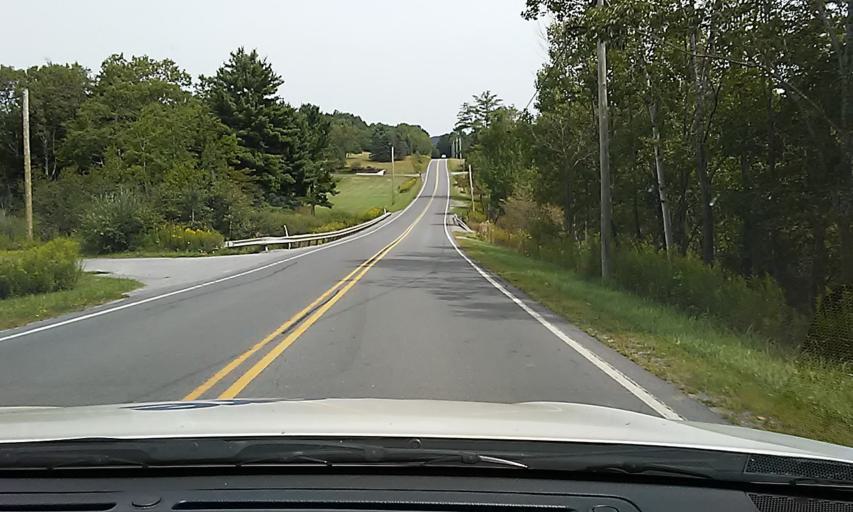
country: US
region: Pennsylvania
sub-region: Elk County
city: Ridgway
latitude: 41.3036
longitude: -78.6635
